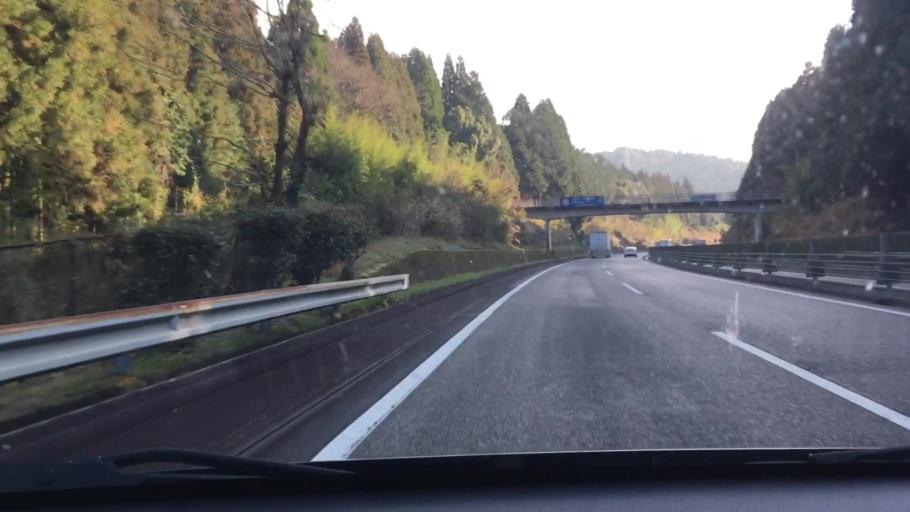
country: JP
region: Kagoshima
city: Okuchi-shinohara
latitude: 31.9988
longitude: 130.7587
